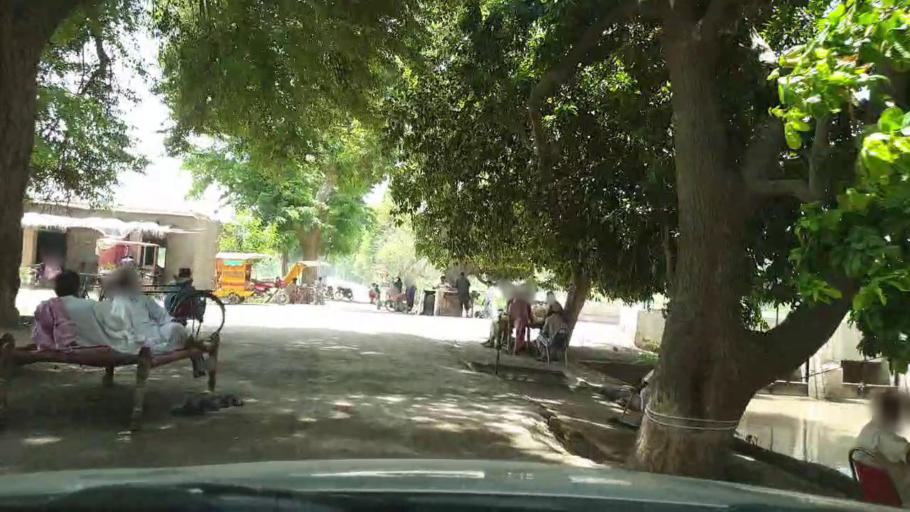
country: PK
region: Sindh
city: Pano Aqil
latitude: 27.8605
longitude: 69.0882
